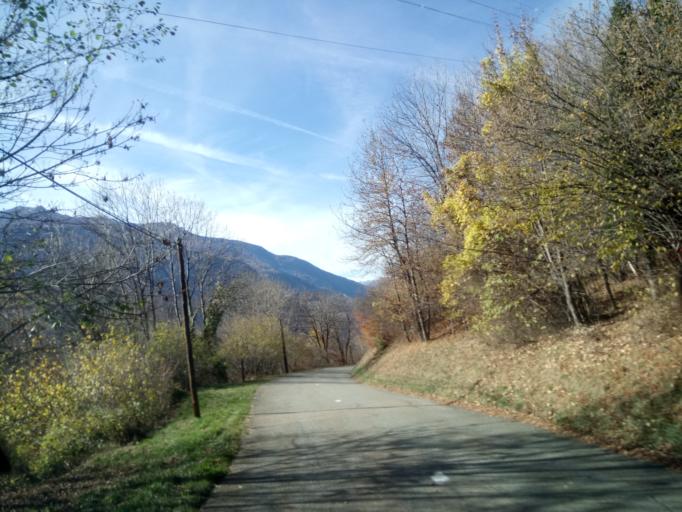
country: FR
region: Rhone-Alpes
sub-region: Departement de la Savoie
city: Saint-Michel-de-Maurienne
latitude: 45.2270
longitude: 6.4770
